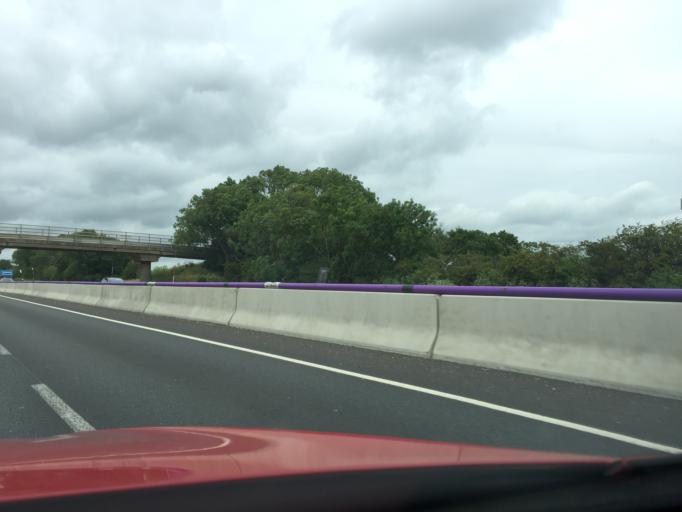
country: GB
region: England
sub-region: Milton Keynes
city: Hanslope
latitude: 52.1307
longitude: -0.8227
